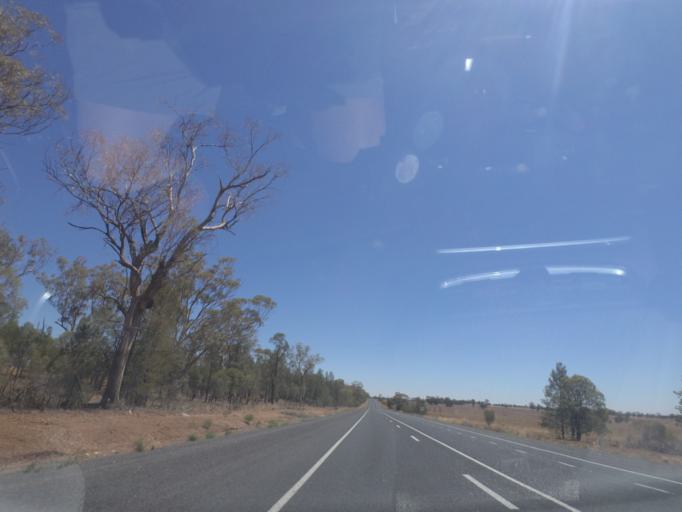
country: AU
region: New South Wales
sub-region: Gilgandra
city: Gilgandra
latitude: -31.4883
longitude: 148.8759
